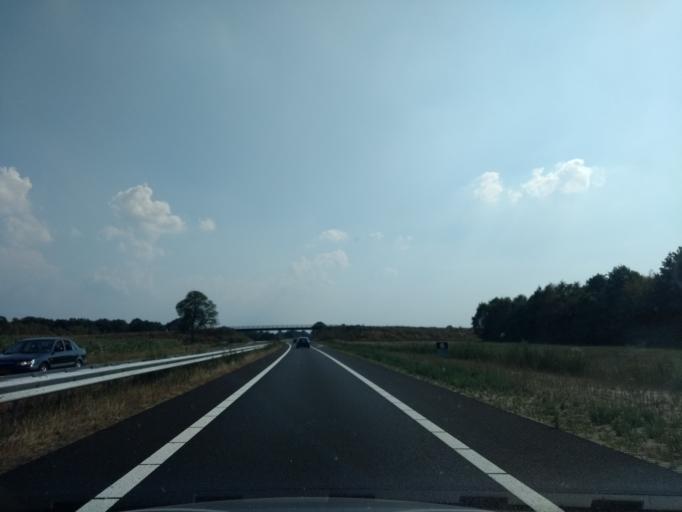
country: NL
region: Overijssel
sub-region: Gemeente Haaksbergen
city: Haaksbergen
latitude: 52.1477
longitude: 6.6824
